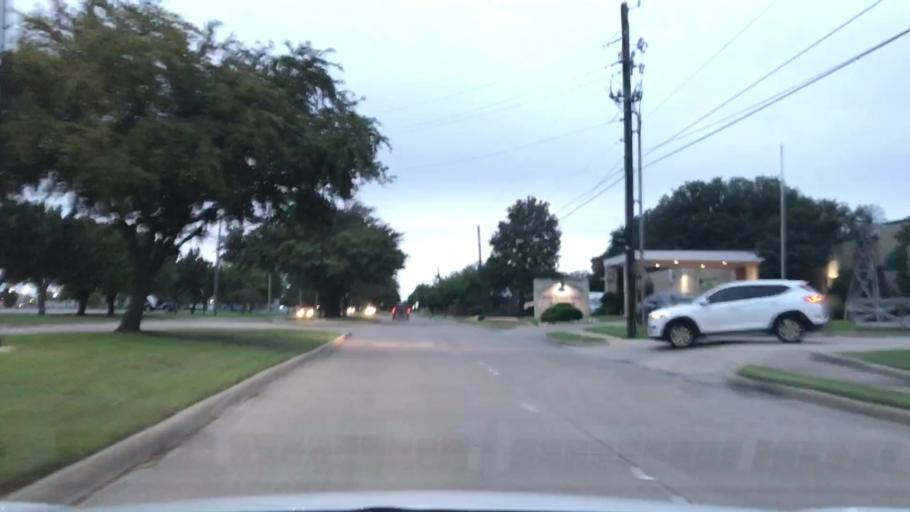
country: US
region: Texas
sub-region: Dallas County
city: Garland
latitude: 32.8465
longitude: -96.6190
